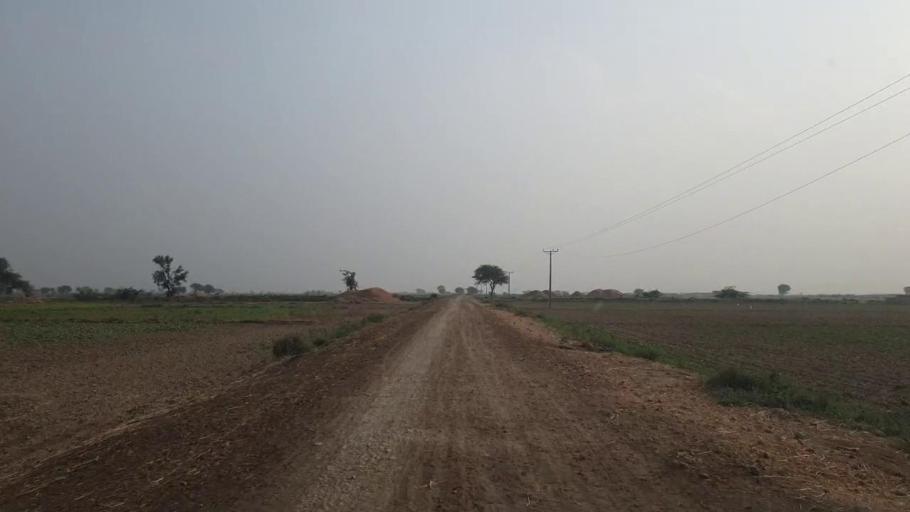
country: PK
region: Sindh
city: Mirpur Batoro
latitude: 24.5490
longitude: 68.4208
